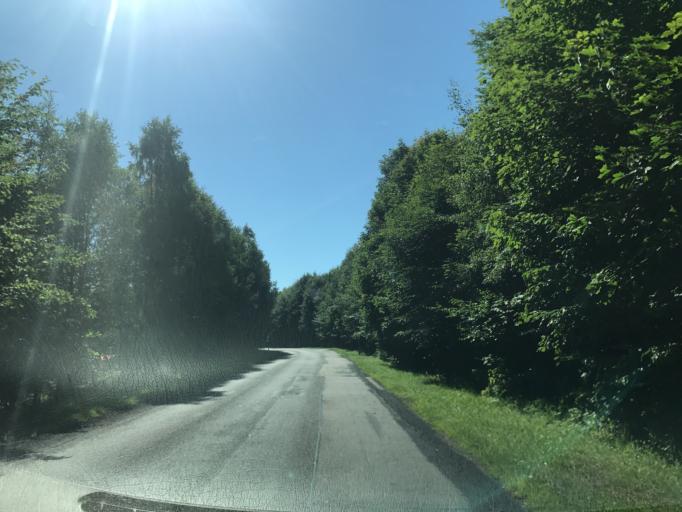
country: PL
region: Pomeranian Voivodeship
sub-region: Powiat bytowski
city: Czarna Dabrowka
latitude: 54.3769
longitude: 17.4944
